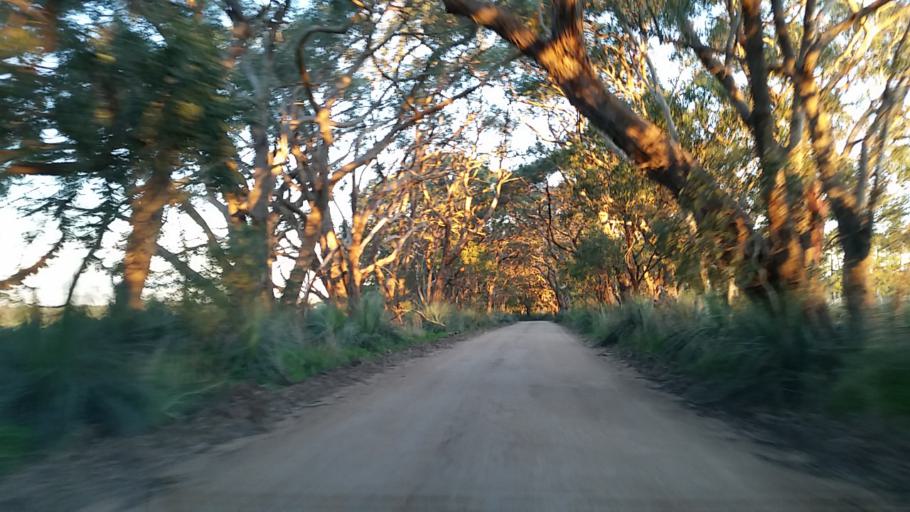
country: AU
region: South Australia
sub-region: Alexandrina
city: Mount Compass
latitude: -35.2838
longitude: 138.5996
